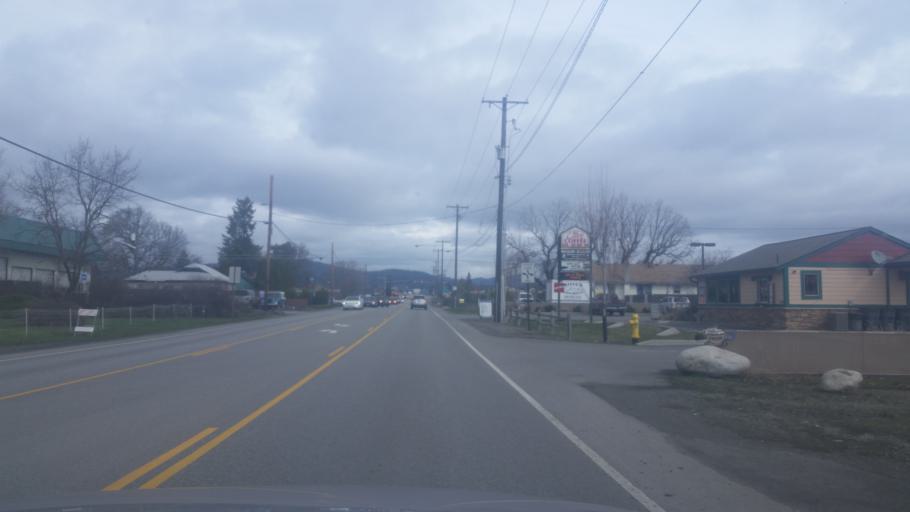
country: US
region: Washington
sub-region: Spokane County
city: Liberty Lake
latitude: 47.6617
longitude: -117.1536
